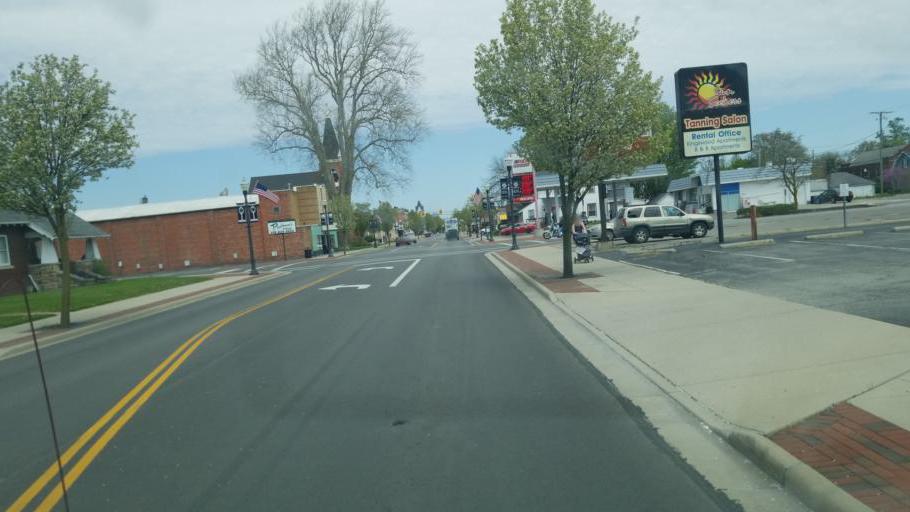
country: US
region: Ohio
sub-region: Hardin County
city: Ada
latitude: 40.7681
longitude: -83.8231
